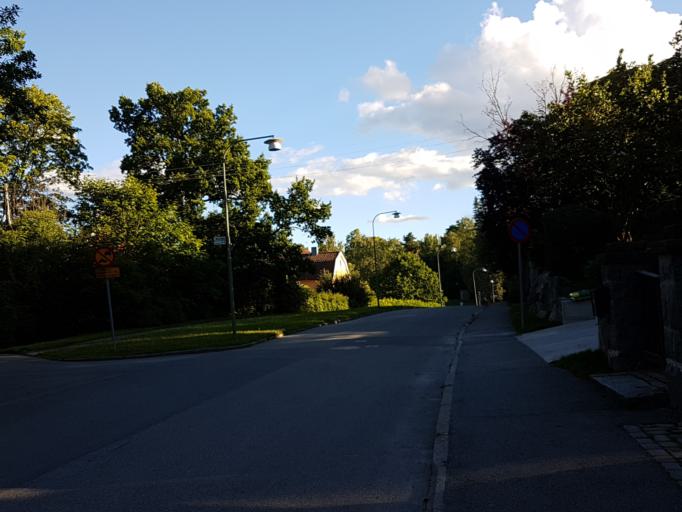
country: SE
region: Stockholm
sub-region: Stockholms Kommun
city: Bromma
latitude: 59.3262
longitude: 17.9715
